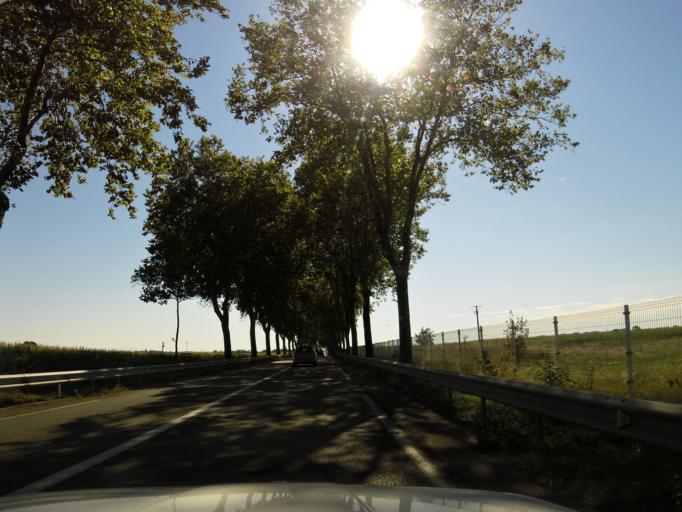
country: FR
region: Rhone-Alpes
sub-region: Departement de l'Ain
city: Leyment
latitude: 45.9302
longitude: 5.2857
